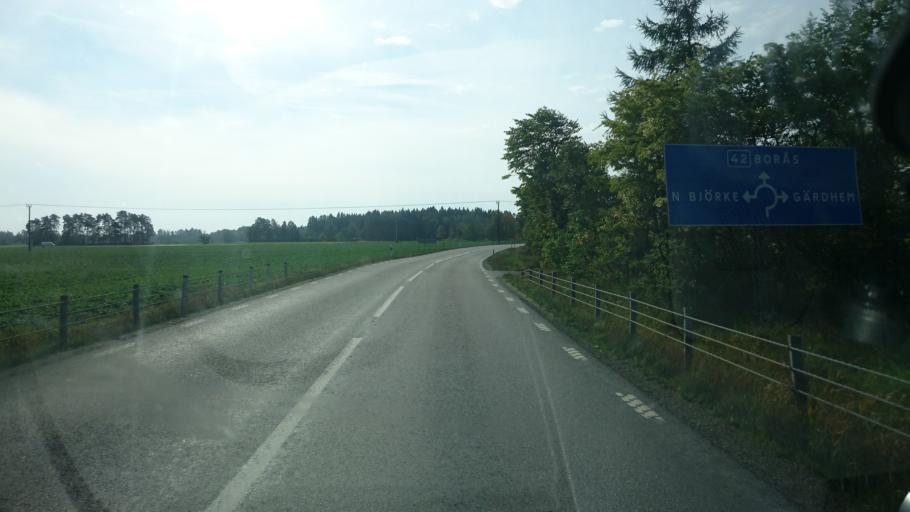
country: SE
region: Vaestra Goetaland
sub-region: Vanersborgs Kommun
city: Vargon
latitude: 58.2671
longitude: 12.4009
